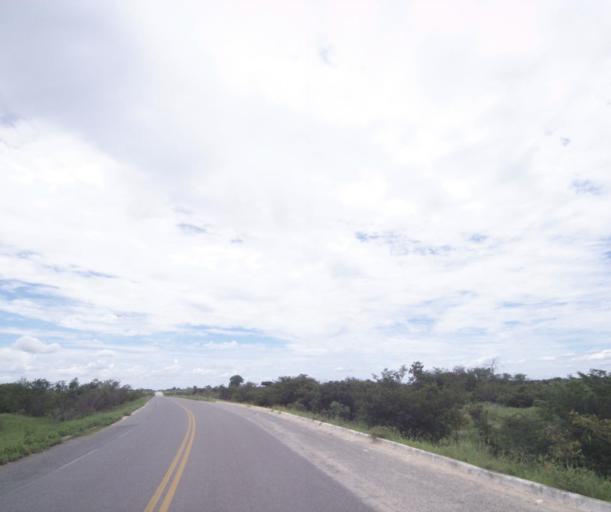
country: BR
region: Bahia
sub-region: Carinhanha
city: Carinhanha
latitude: -14.2909
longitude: -43.7856
